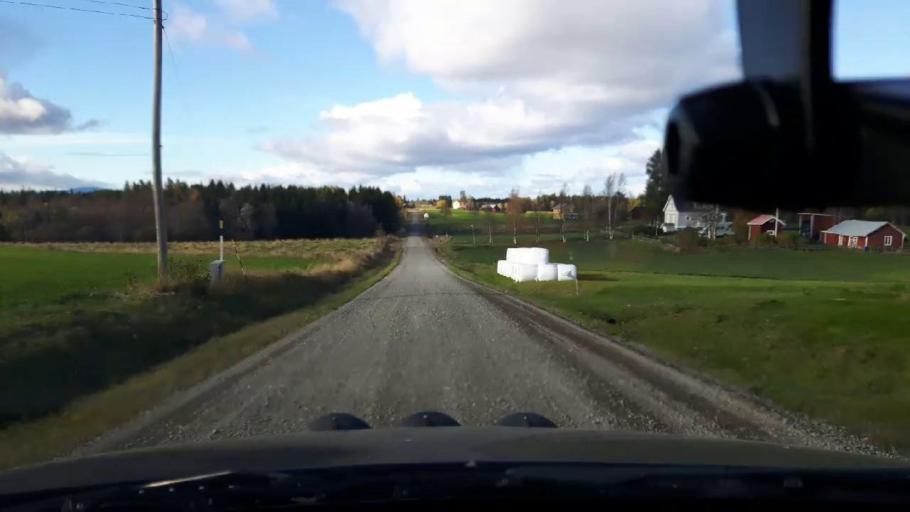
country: SE
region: Jaemtland
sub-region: Bergs Kommun
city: Hoverberg
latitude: 63.0210
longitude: 14.3026
